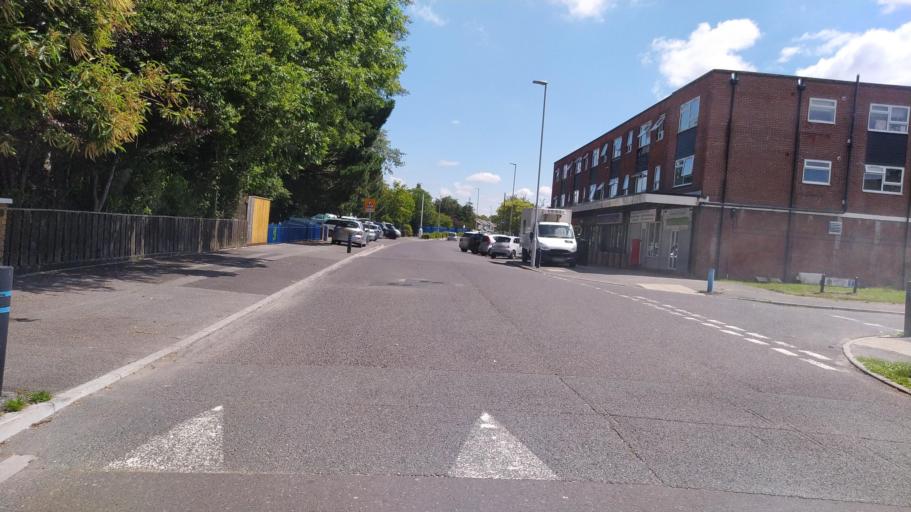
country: GB
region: England
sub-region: Poole
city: Poole
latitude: 50.7254
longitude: -2.0282
